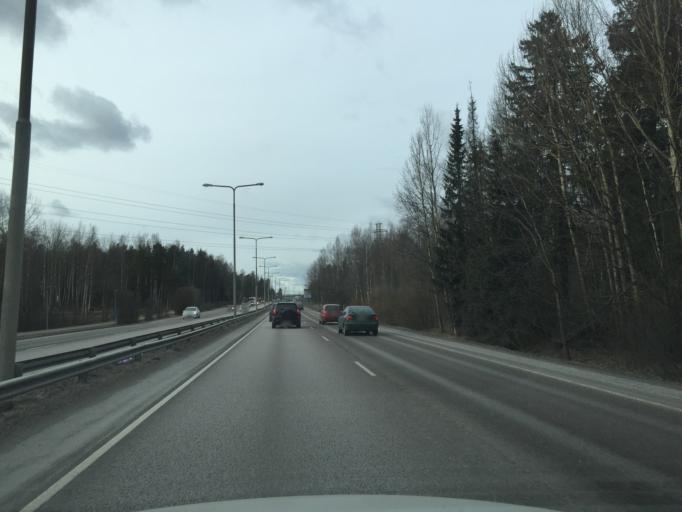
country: FI
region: Uusimaa
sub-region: Helsinki
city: Teekkarikylae
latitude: 60.2558
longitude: 24.8808
